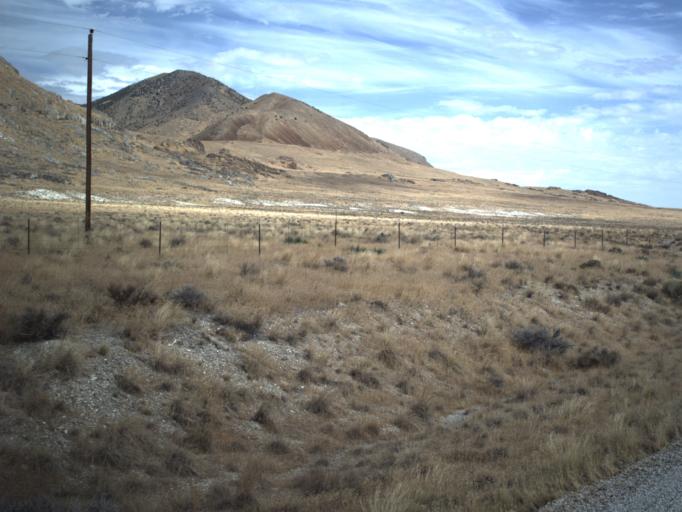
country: US
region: Utah
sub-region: Tooele County
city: Wendover
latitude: 41.4450
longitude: -113.6860
